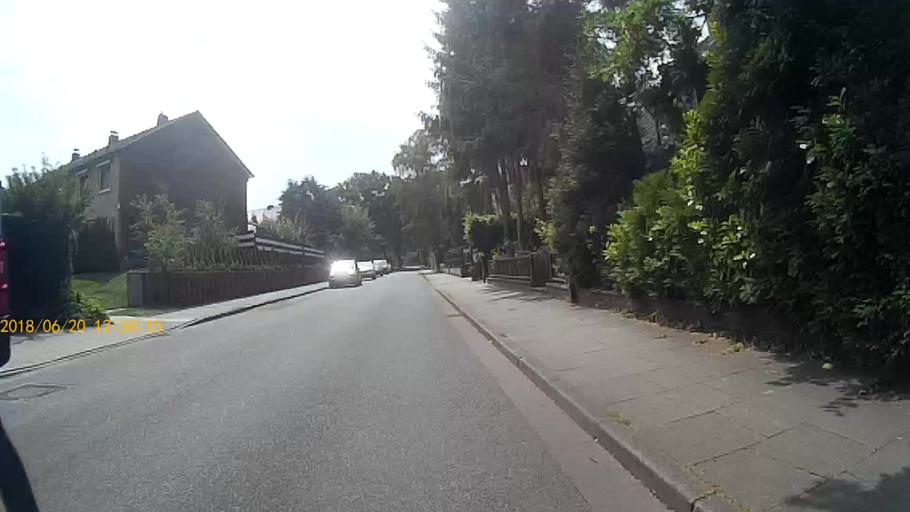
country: DE
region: Lower Saxony
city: Neu Wulmstorf
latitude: 53.4752
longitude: 9.8595
